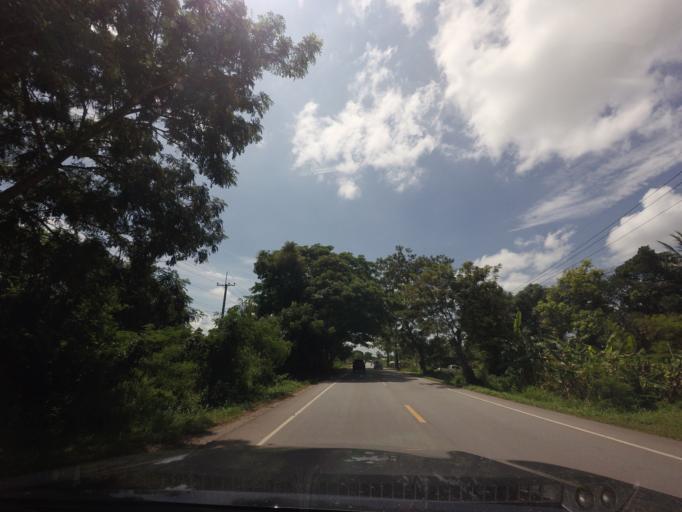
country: TH
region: Changwat Udon Thani
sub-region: Amphoe Ban Phue
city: Ban Phue
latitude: 17.7378
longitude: 102.3972
